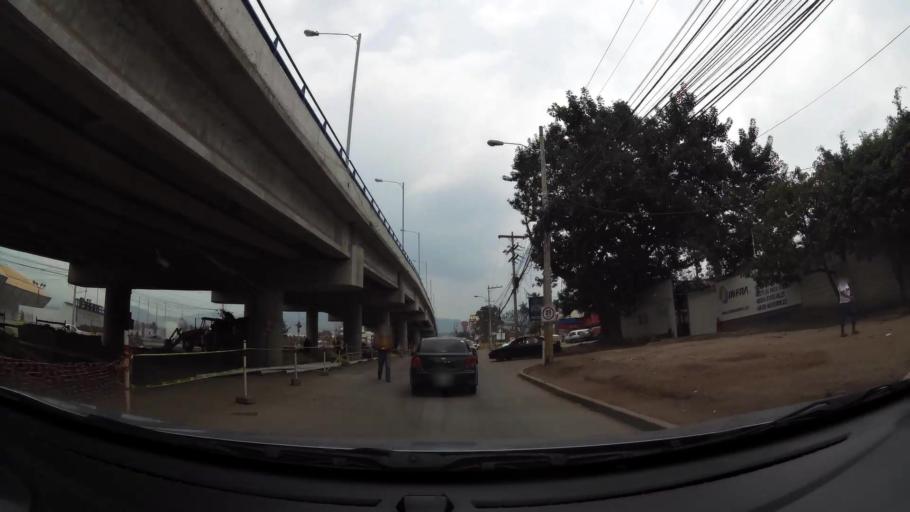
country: HN
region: Francisco Morazan
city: Tegucigalpa
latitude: 14.0838
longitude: -87.1704
